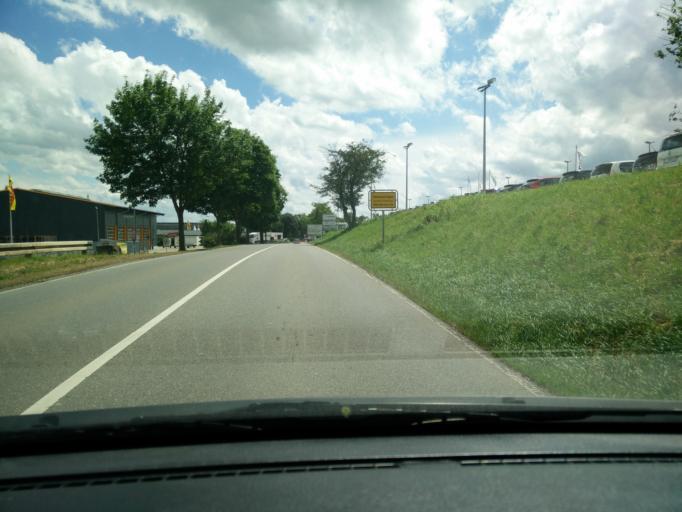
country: DE
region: Baden-Wuerttemberg
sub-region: Freiburg Region
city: Donaueschingen
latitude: 47.9648
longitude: 8.5054
